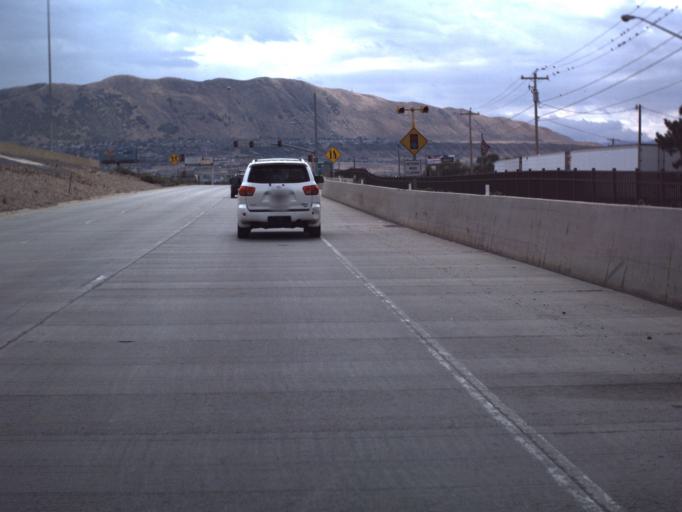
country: US
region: Utah
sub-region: Salt Lake County
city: Draper
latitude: 40.5261
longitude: -111.8919
